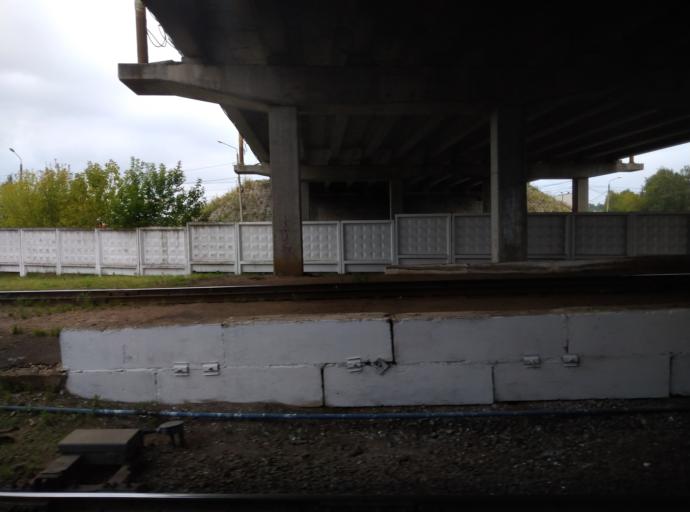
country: RU
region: Kostroma
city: Oktyabr'skiy
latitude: 57.7556
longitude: 40.9796
